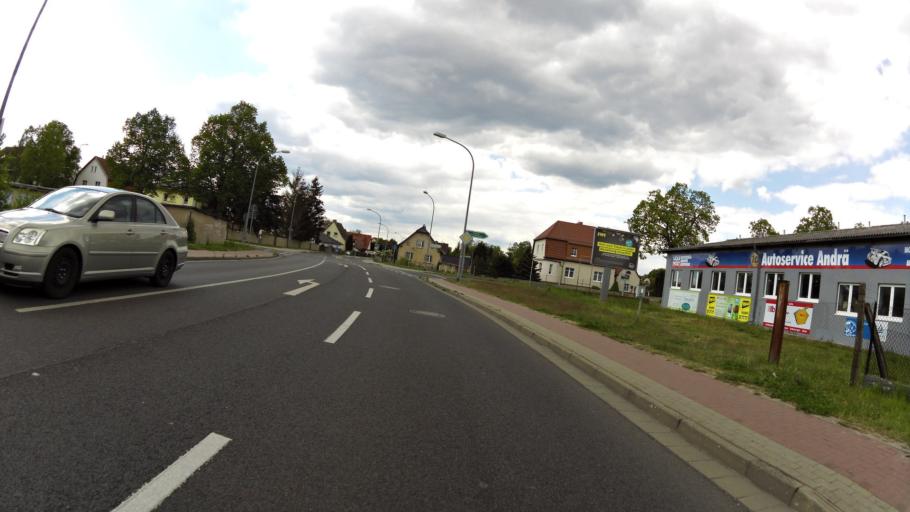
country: DE
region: Brandenburg
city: Furstenwalde
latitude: 52.3783
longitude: 14.0629
